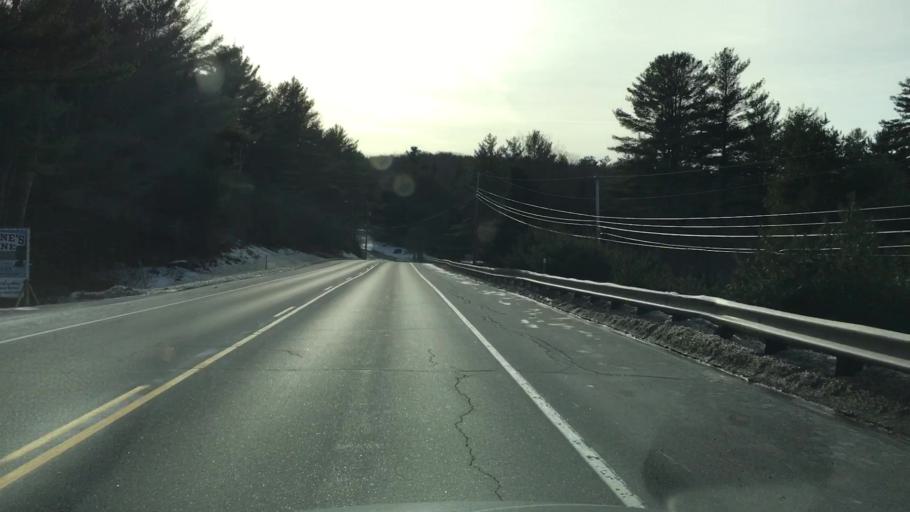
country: US
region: New Hampshire
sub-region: Sullivan County
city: Sunapee
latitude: 43.3796
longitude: -72.1055
